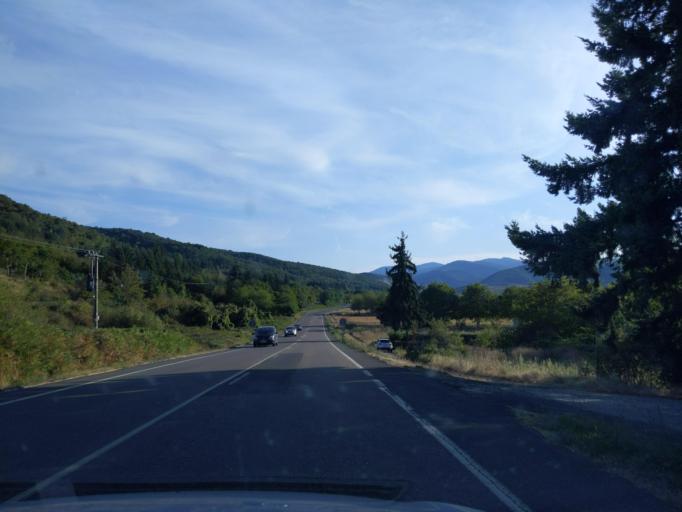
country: ES
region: La Rioja
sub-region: Provincia de La Rioja
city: Santurdejo
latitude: 42.3697
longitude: -2.9812
